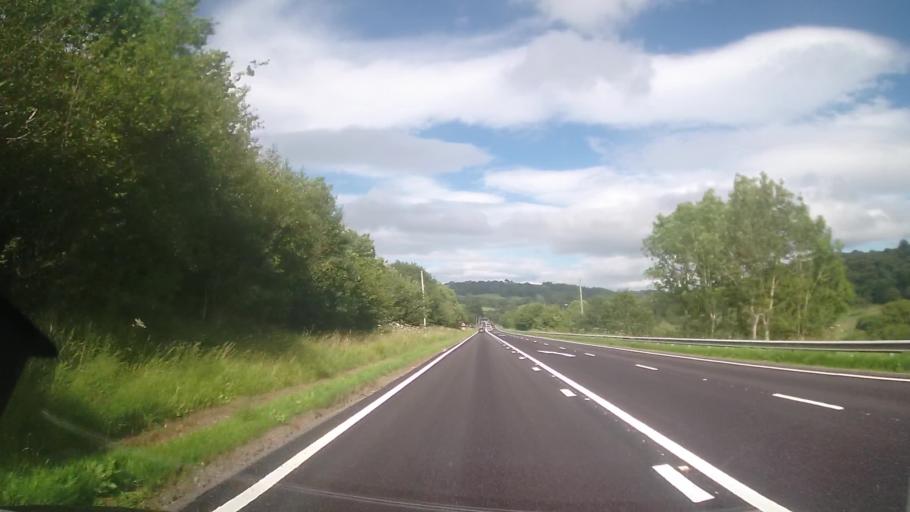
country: GB
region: Wales
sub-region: Conwy
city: Llangwm
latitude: 52.9883
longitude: -3.4887
